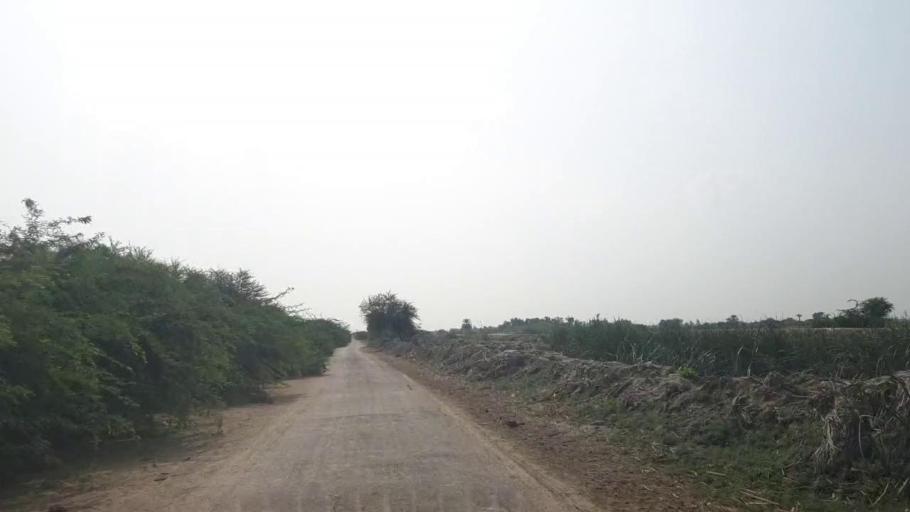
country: PK
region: Sindh
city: Badin
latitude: 24.7220
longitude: 68.7347
